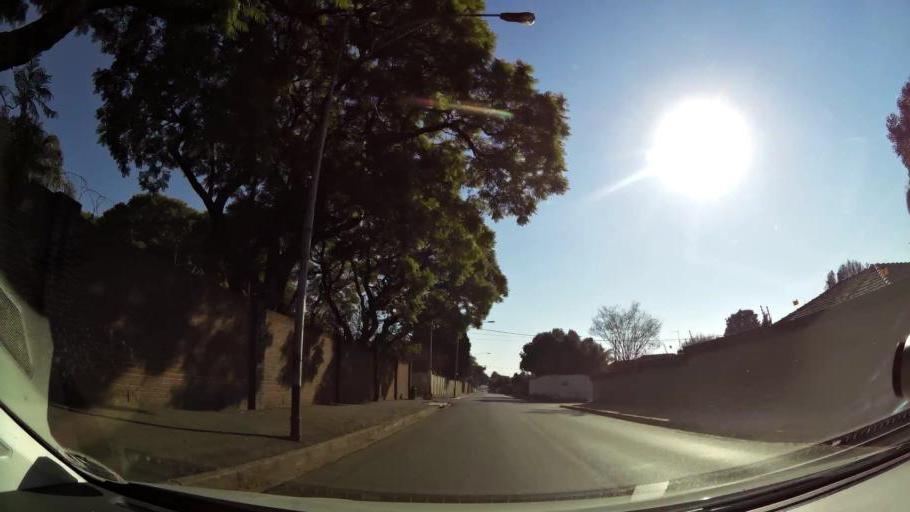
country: ZA
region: Gauteng
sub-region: City of Johannesburg Metropolitan Municipality
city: Johannesburg
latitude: -26.1541
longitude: 28.0962
